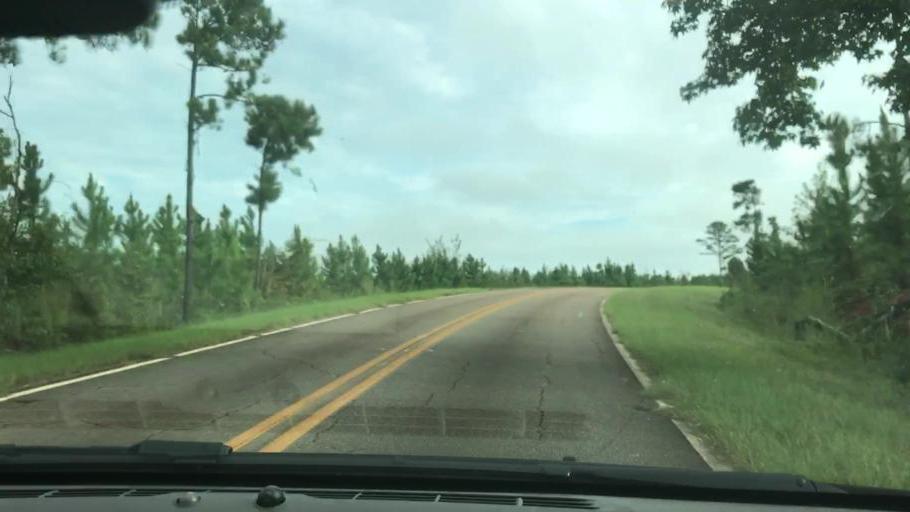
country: US
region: Georgia
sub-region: Stewart County
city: Lumpkin
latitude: 32.0599
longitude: -84.9038
